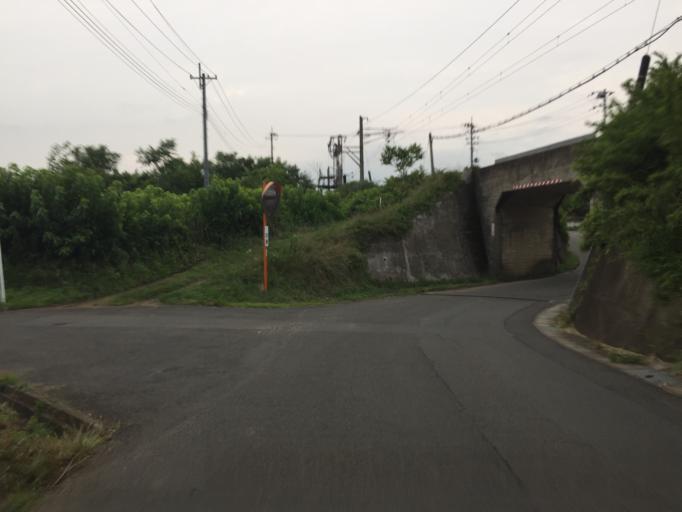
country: JP
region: Fukushima
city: Fukushima-shi
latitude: 37.7147
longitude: 140.4564
